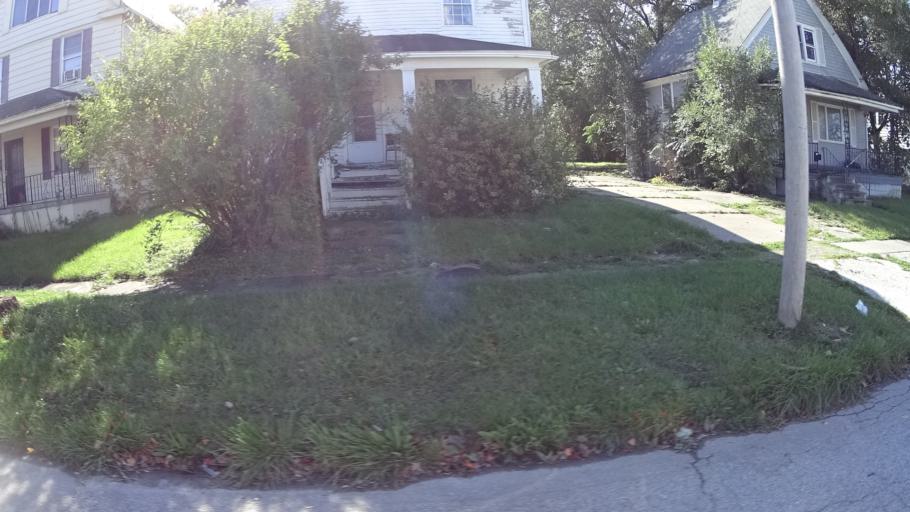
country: US
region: Ohio
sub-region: Lorain County
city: Lorain
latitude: 41.4559
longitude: -82.1784
